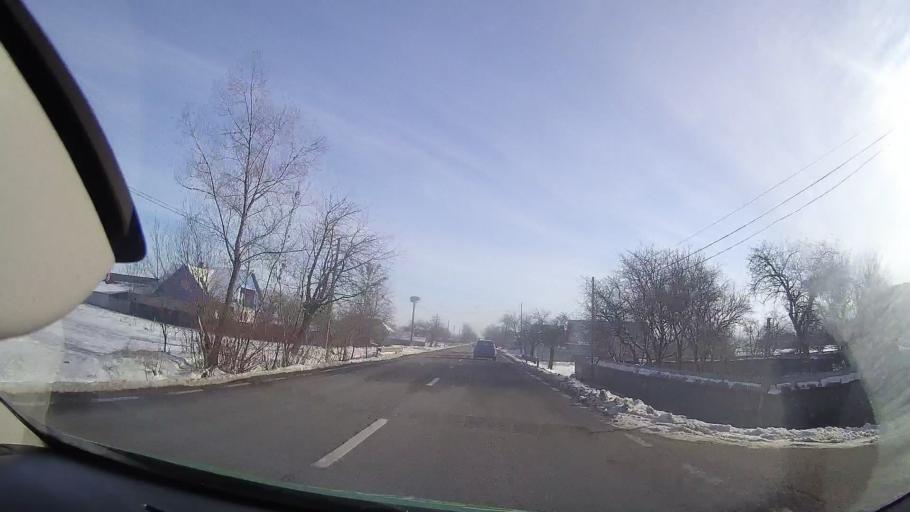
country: RO
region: Neamt
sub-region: Comuna Negresti
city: Negresti
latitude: 47.0605
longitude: 26.3849
